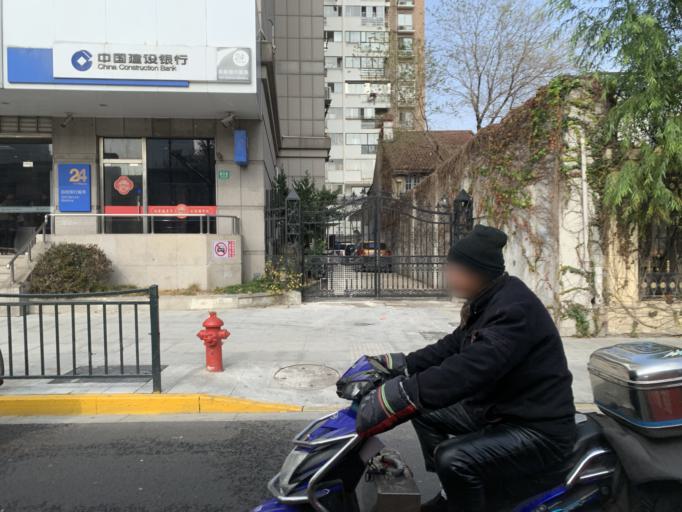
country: CN
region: Shanghai Shi
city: Xuhui
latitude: 31.2020
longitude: 121.4464
